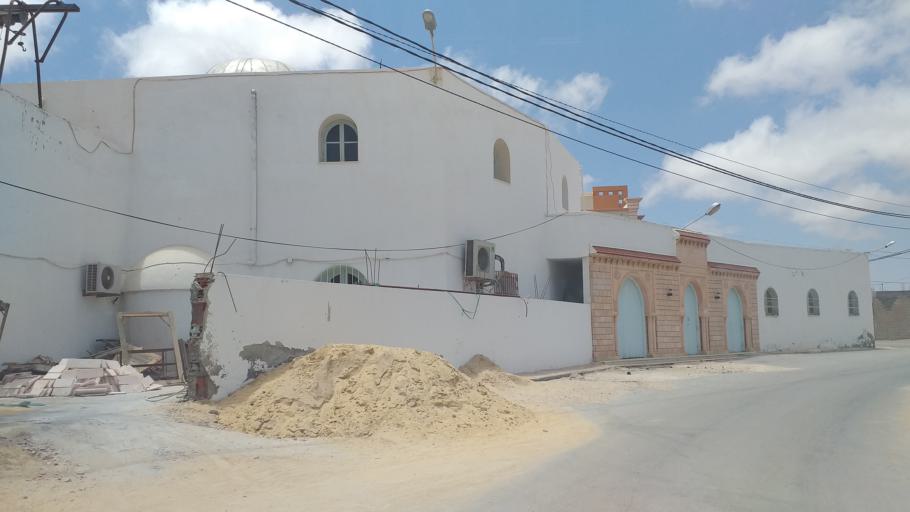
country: TN
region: Qabis
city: Gabes
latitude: 33.9334
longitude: 10.0603
